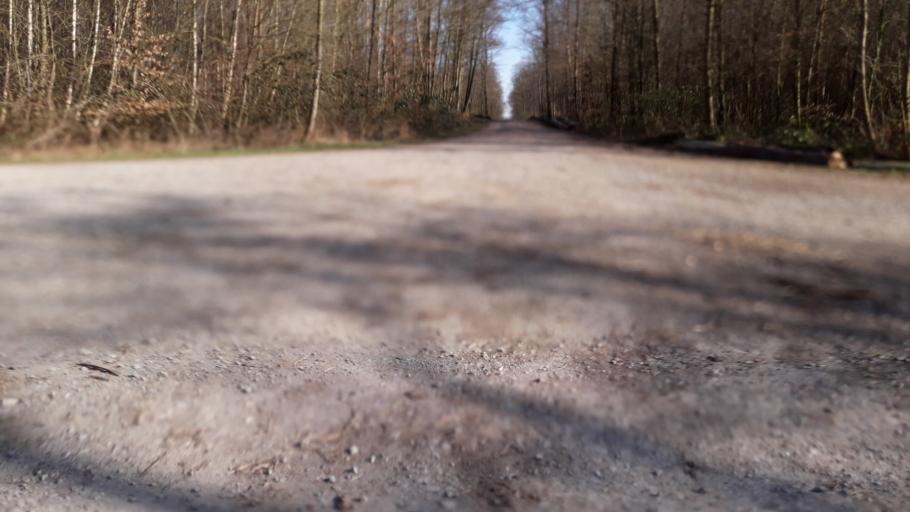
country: DE
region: North Rhine-Westphalia
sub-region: Regierungsbezirk Detmold
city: Salzkotten
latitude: 51.6644
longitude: 8.6656
